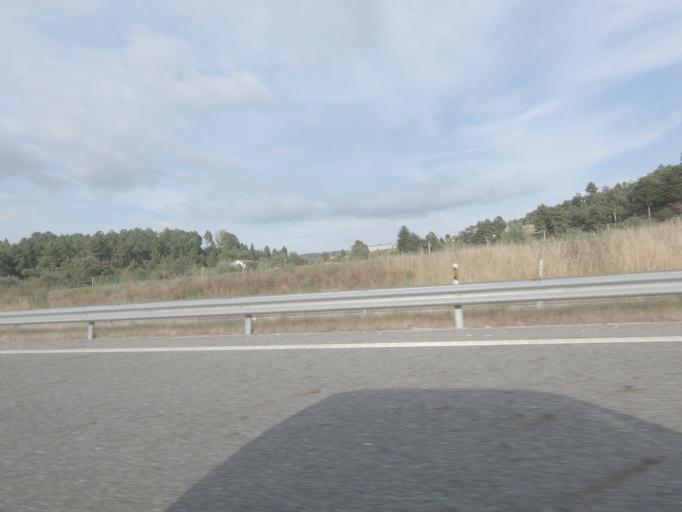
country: PT
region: Vila Real
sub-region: Boticas
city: Boticas
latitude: 41.6564
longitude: -7.5795
